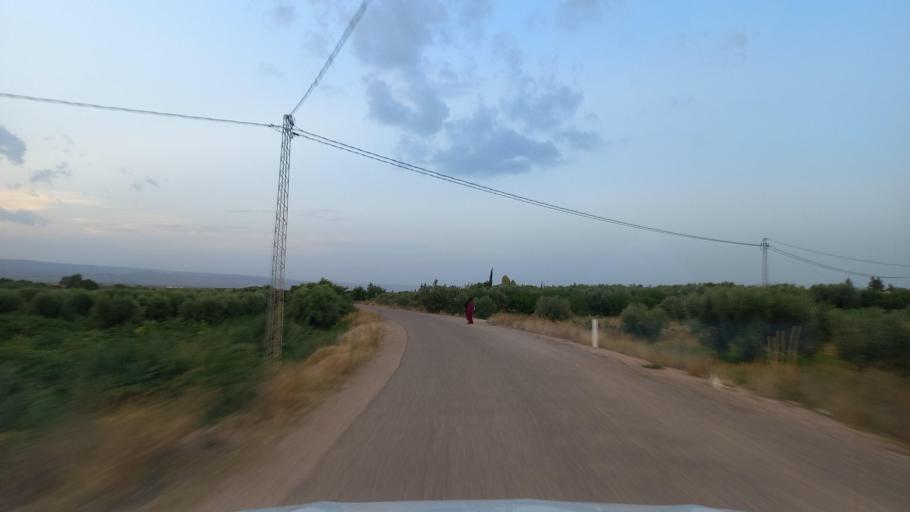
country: TN
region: Al Qasrayn
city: Kasserine
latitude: 35.2684
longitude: 9.0483
